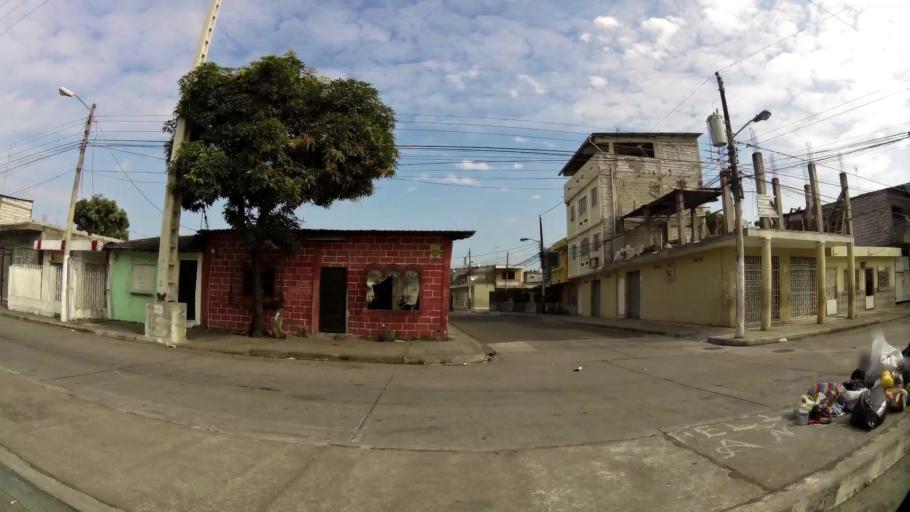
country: EC
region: Guayas
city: Guayaquil
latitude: -2.2570
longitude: -79.8775
